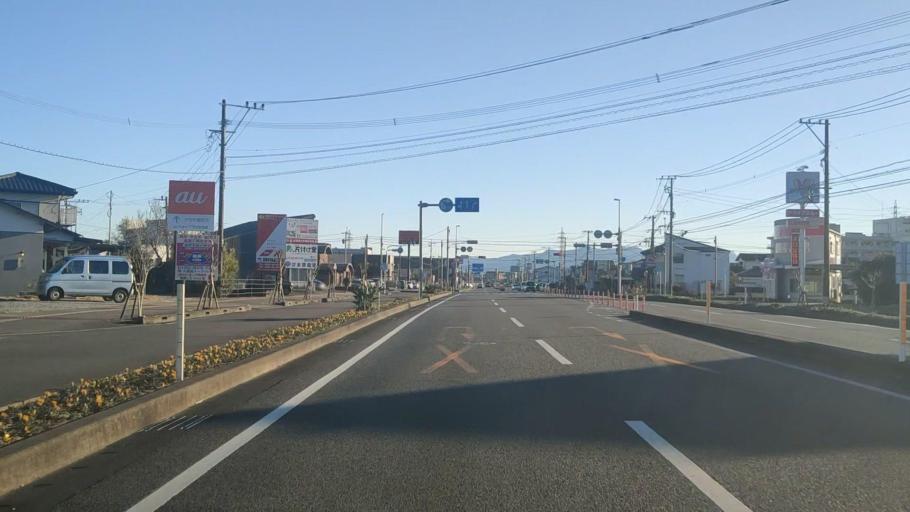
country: JP
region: Miyazaki
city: Miyazaki-shi
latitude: 31.8992
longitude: 131.4062
